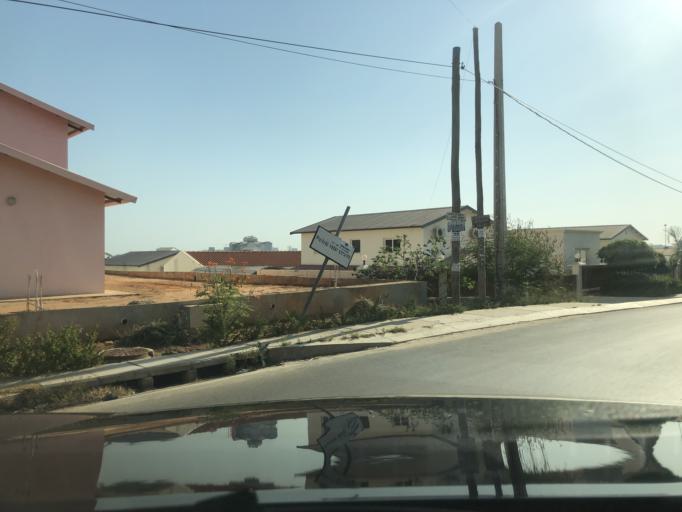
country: AO
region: Luanda
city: Luanda
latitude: -8.9078
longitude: 13.2240
